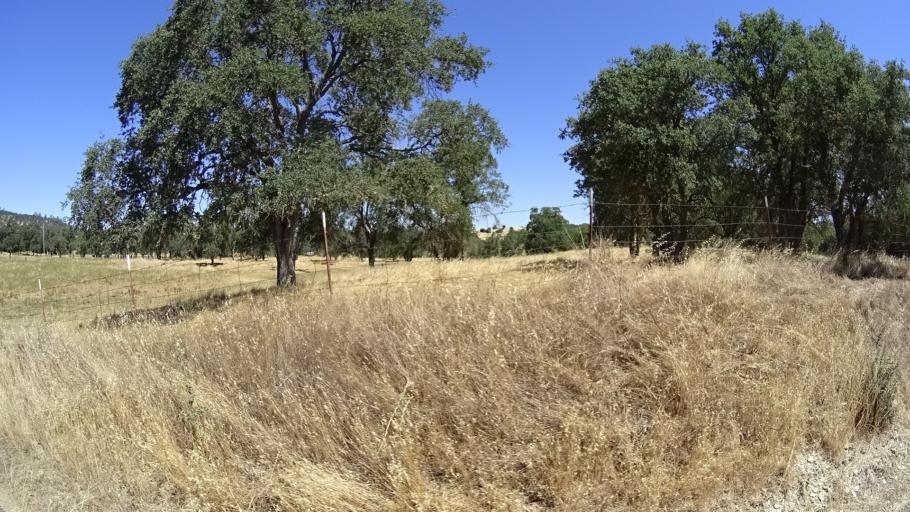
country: US
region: California
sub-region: Calaveras County
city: Copperopolis
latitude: 37.9504
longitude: -120.6873
